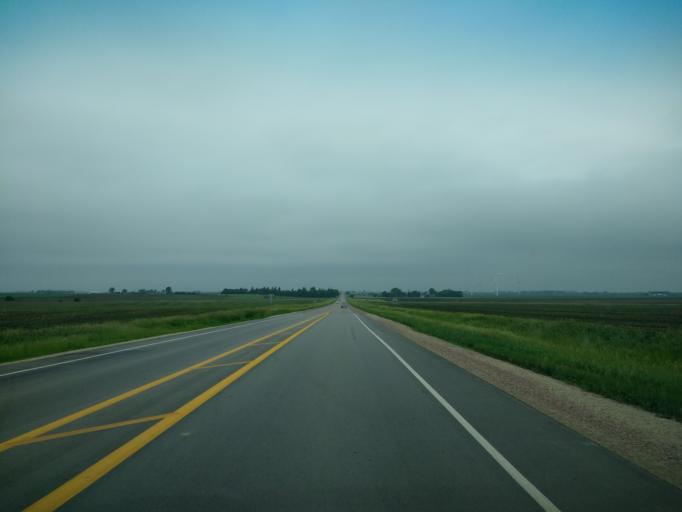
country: US
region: Iowa
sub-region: O'Brien County
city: Sanborn
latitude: 43.1861
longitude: -95.6659
